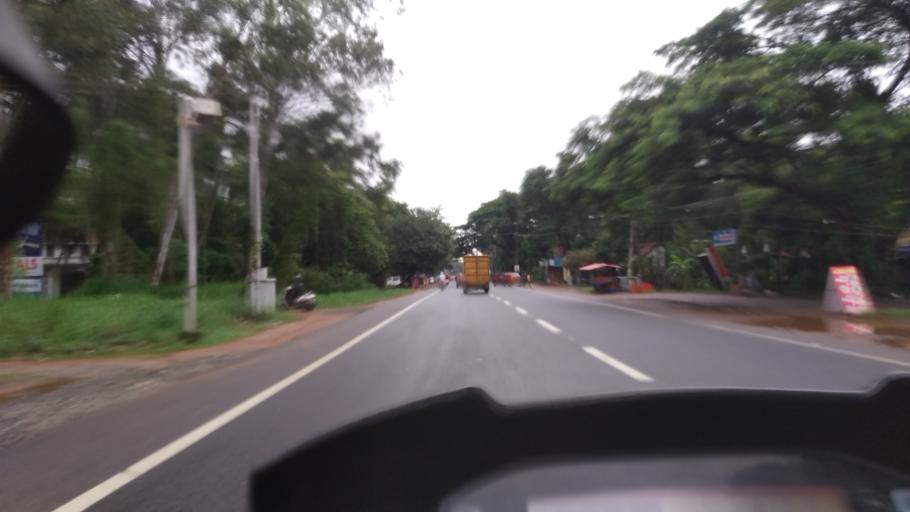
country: IN
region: Kerala
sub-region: Alappuzha
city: Mavelikara
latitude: 9.3140
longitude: 76.4287
